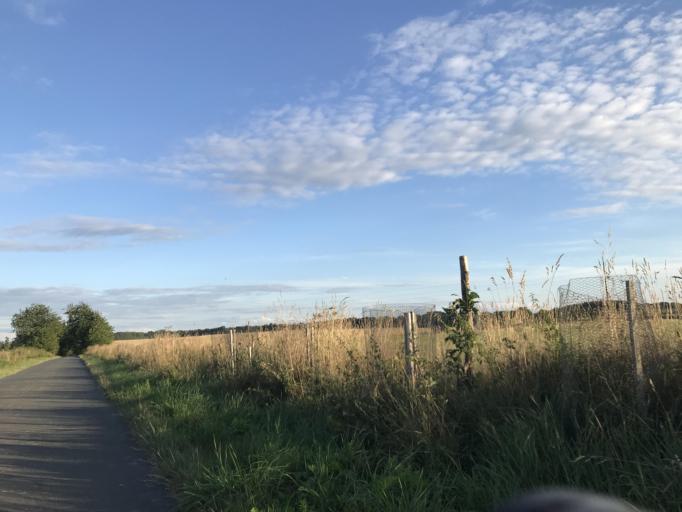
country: DE
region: Lower Saxony
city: Reinstorf
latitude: 53.2367
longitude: 10.5902
